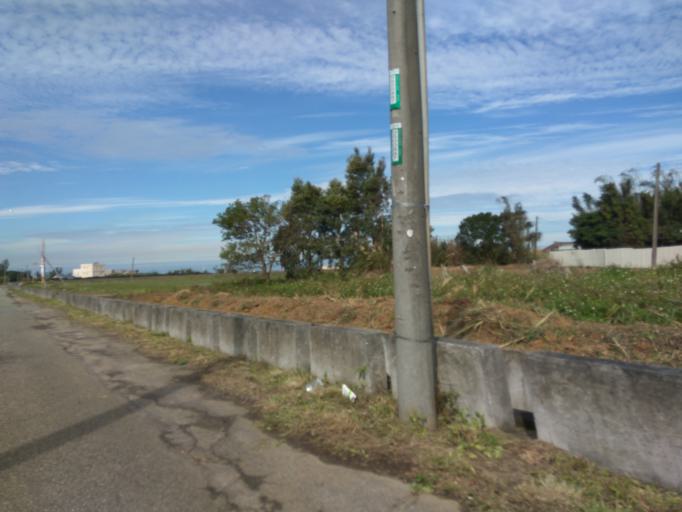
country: TW
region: Taiwan
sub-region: Hsinchu
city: Zhubei
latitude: 25.0063
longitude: 121.0780
